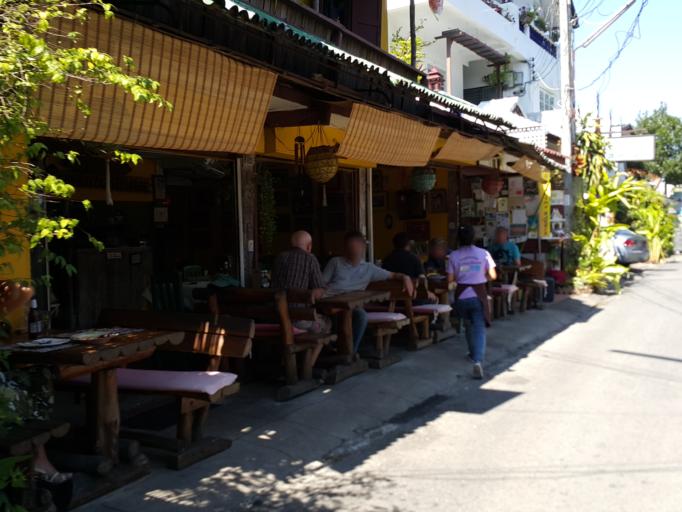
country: TH
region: Chiang Mai
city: Chiang Mai
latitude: 18.7884
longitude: 98.9909
